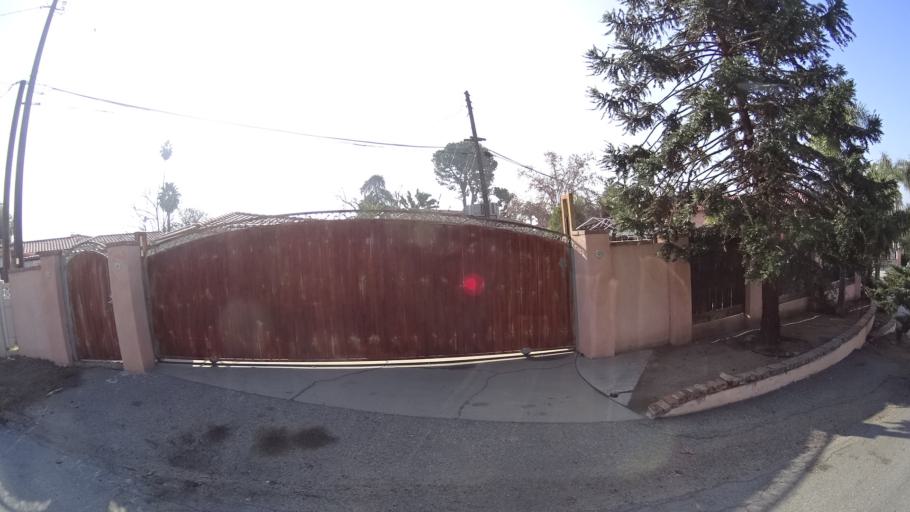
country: US
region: California
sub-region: Kern County
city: Oildale
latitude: 35.4014
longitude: -118.9873
